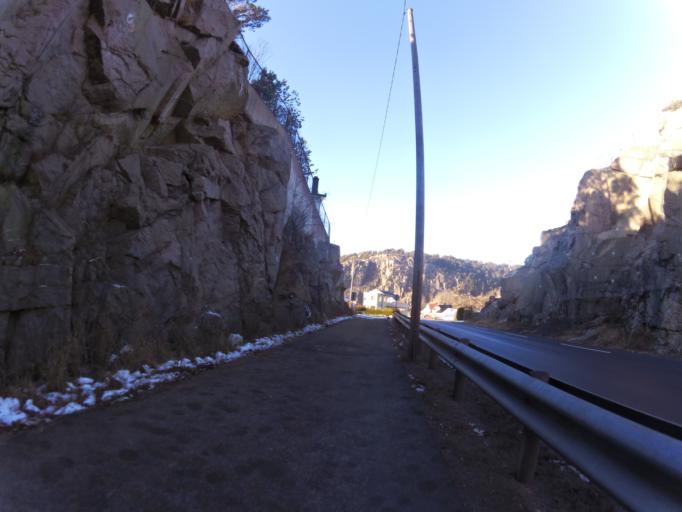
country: NO
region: Ostfold
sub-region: Fredrikstad
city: Lervik
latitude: 59.2080
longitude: 10.8050
